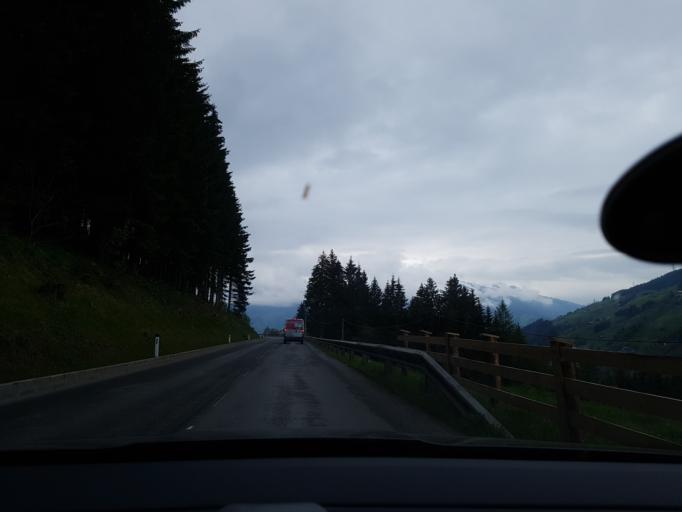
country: AT
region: Tyrol
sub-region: Politischer Bezirk Schwaz
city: Gerlosberg
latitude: 47.2116
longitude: 11.9434
